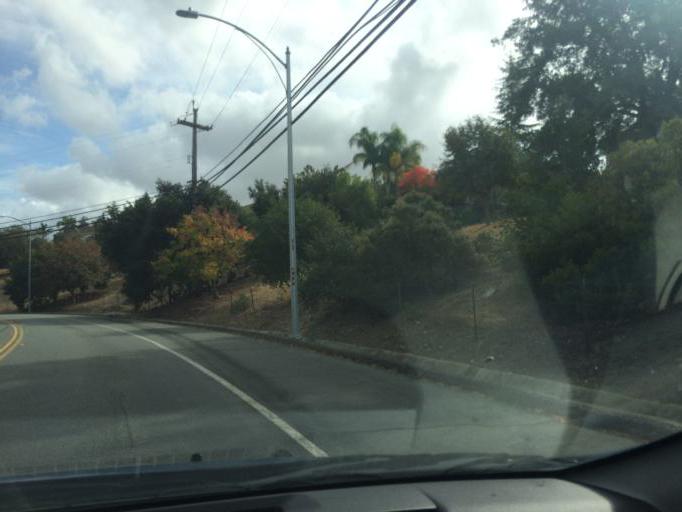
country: US
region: California
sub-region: Santa Clara County
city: Seven Trees
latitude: 37.2800
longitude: -121.7573
